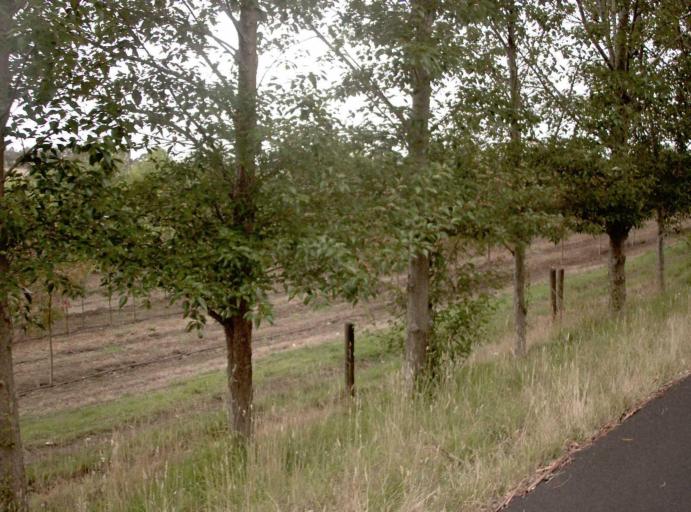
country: AU
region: Victoria
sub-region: Cardinia
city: Bunyip
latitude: -38.2130
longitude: 145.7538
